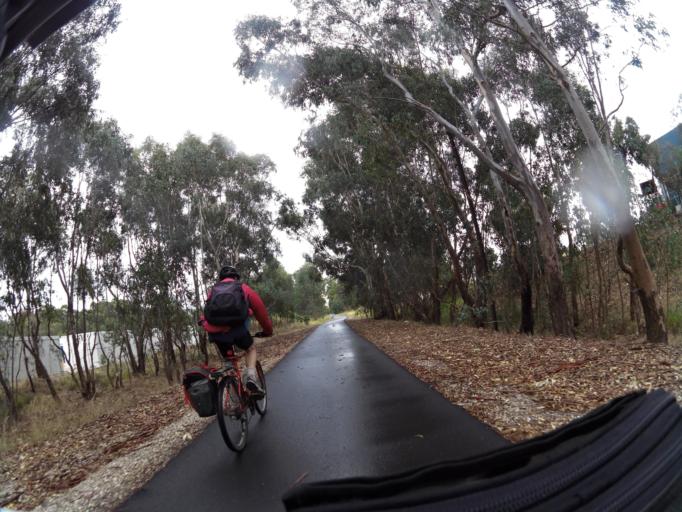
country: AU
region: Victoria
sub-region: Wodonga
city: Wodonga
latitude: -36.1374
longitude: 146.9057
